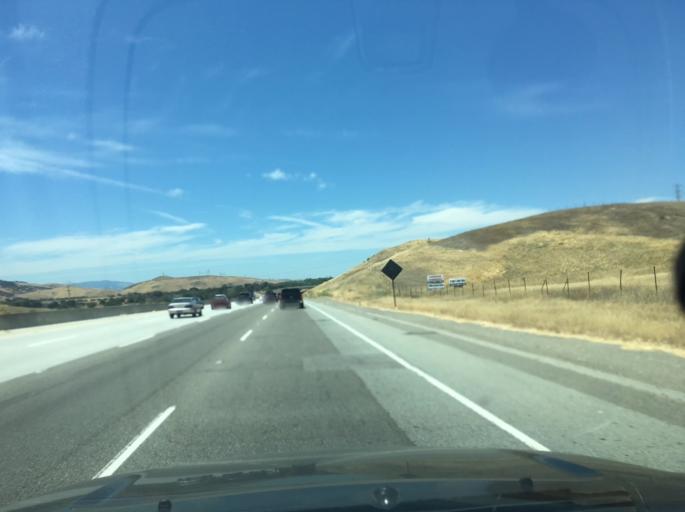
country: US
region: California
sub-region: Santa Clara County
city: Morgan Hill
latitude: 37.2034
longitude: -121.7122
